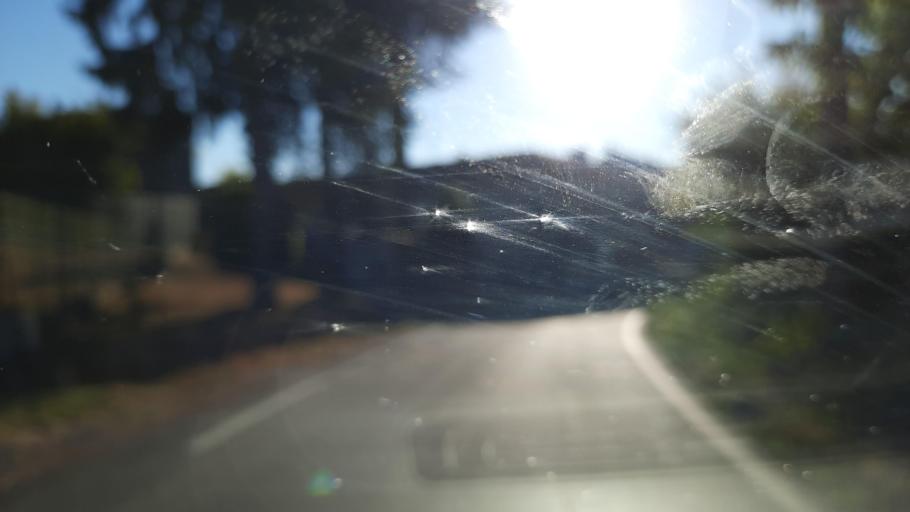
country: IT
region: Piedmont
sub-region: Provincia di Alessandria
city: Vignale Monferrato
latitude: 45.0098
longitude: 8.4023
